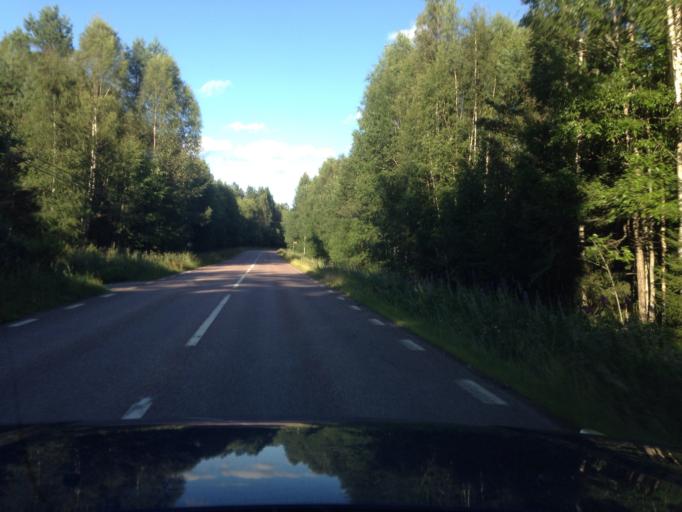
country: SE
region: Dalarna
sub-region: Ludvika Kommun
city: Grangesberg
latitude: 60.1400
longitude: 15.0679
